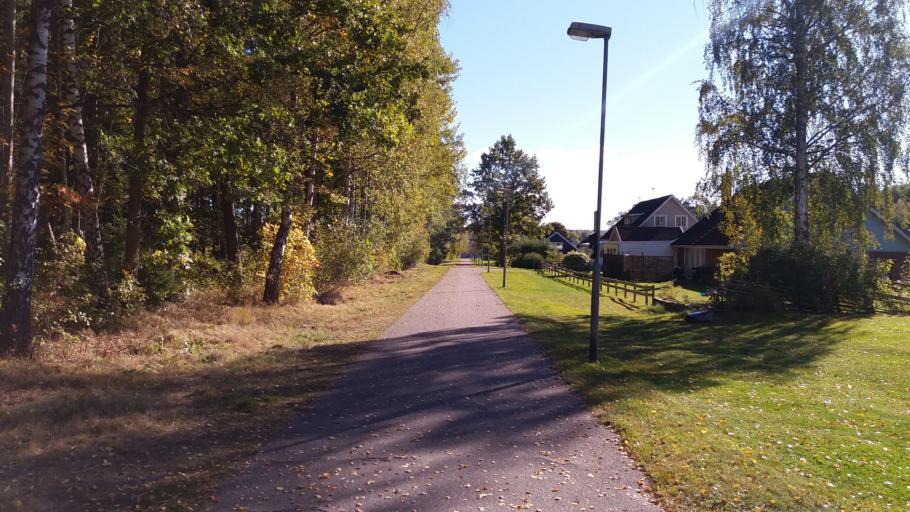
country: SE
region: OErebro
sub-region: Hallsbergs Kommun
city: Skollersta
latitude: 59.1387
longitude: 15.3338
